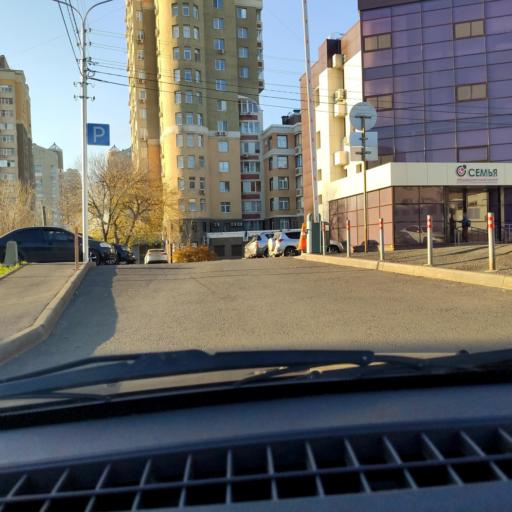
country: RU
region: Bashkortostan
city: Ufa
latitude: 54.7676
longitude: 56.0159
